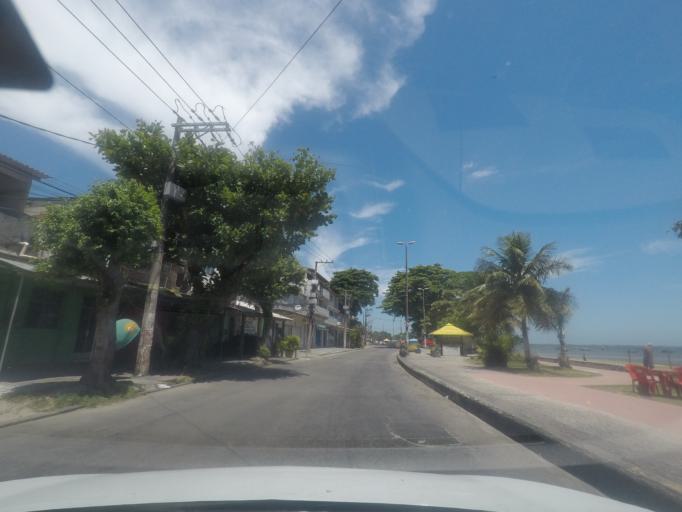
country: BR
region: Rio de Janeiro
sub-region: Itaguai
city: Itaguai
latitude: -22.9846
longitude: -43.6954
